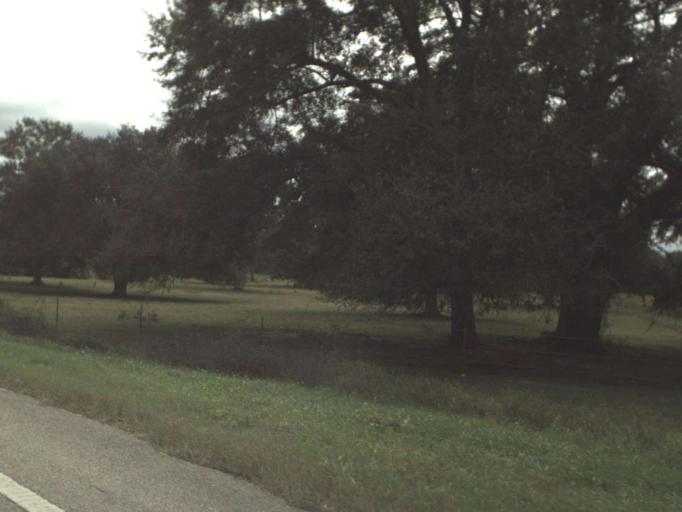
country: US
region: Florida
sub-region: Jackson County
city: Marianna
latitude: 30.6703
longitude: -85.2372
